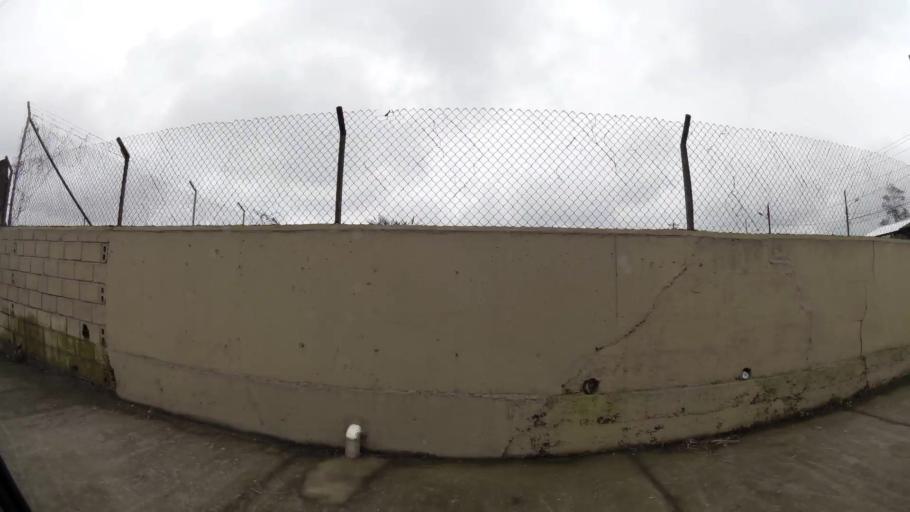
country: EC
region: Santo Domingo de los Tsachilas
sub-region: Canton Santo Domingo de los Colorados
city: Santo Domingo de los Colorados
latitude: -0.2482
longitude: -79.1435
